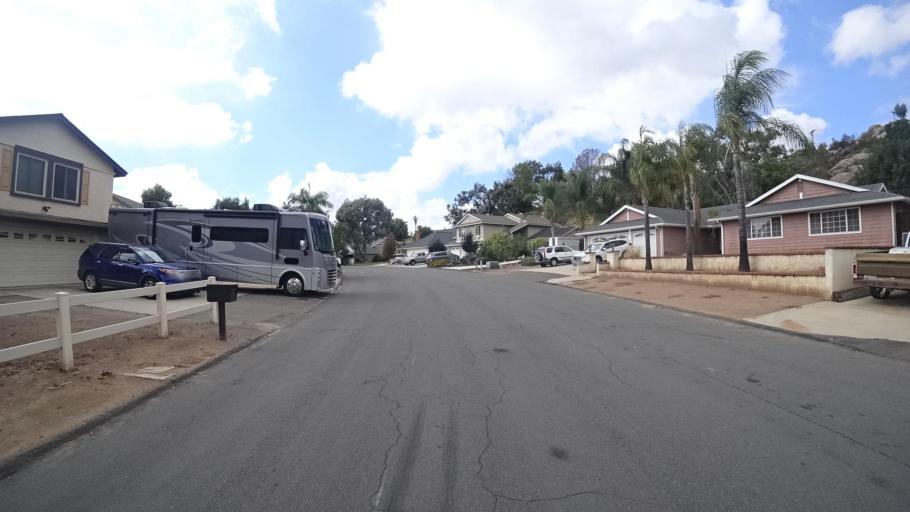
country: US
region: California
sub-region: San Diego County
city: Rancho San Diego
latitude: 32.7686
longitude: -116.9180
